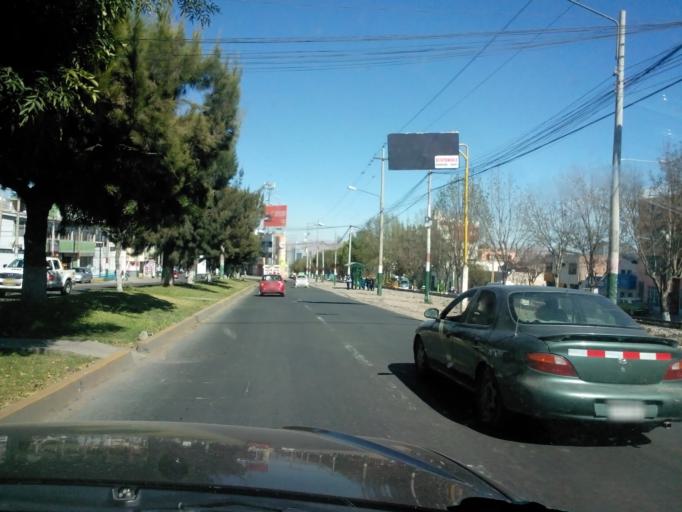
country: PE
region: Arequipa
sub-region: Provincia de Arequipa
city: Arequipa
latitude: -16.3731
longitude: -71.5592
